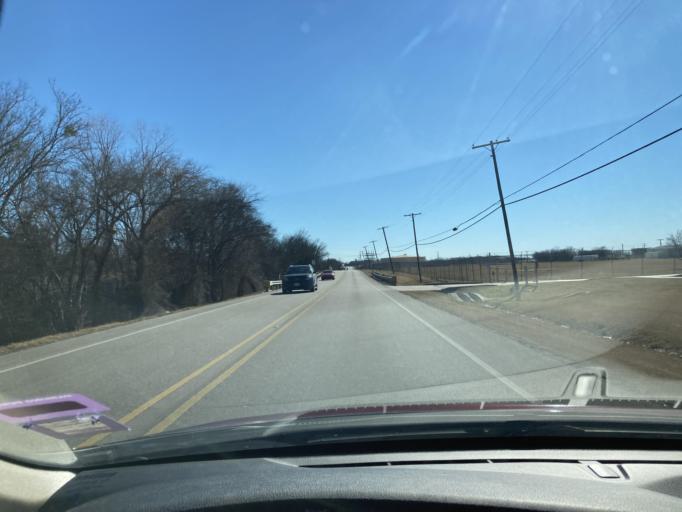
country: US
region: Texas
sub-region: Navarro County
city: Corsicana
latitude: 32.0768
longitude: -96.4632
